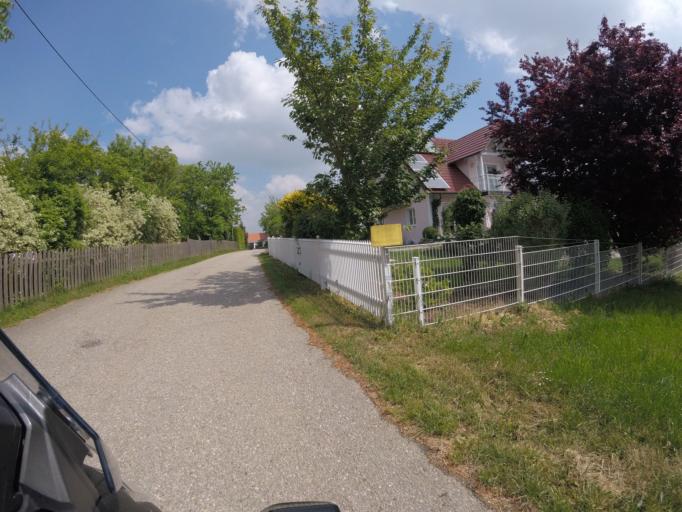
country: DE
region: Bavaria
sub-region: Upper Bavaria
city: Schweitenkirchen
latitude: 48.5126
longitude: 11.6376
